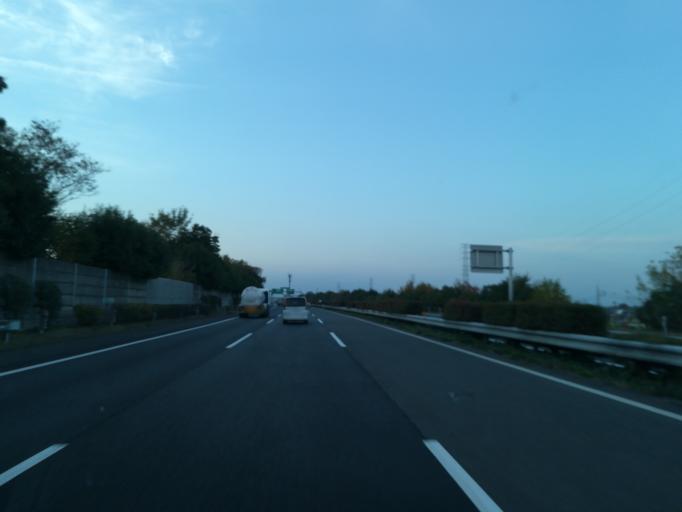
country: JP
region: Gunma
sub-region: Sawa-gun
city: Tamamura
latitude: 36.3142
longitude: 139.0851
